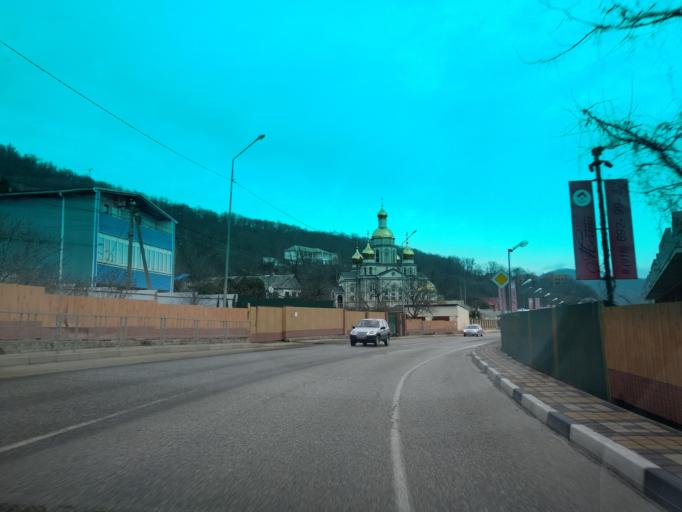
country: RU
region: Krasnodarskiy
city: Ol'ginka
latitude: 44.2031
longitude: 38.8865
